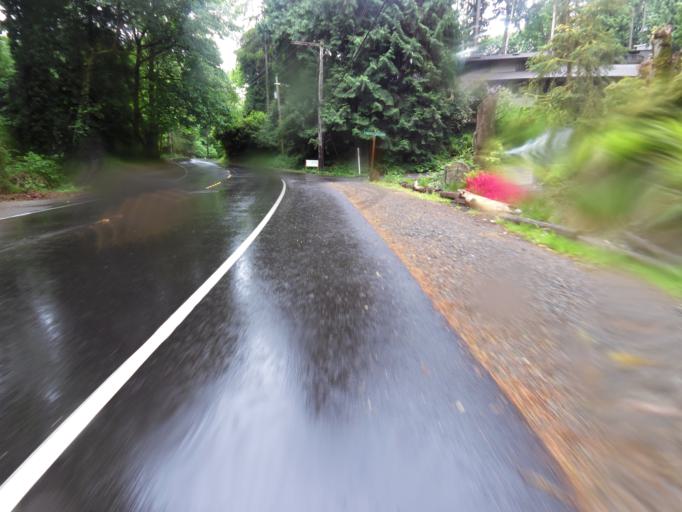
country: US
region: Washington
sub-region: King County
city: Mercer Island
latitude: 47.5593
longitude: -122.2139
